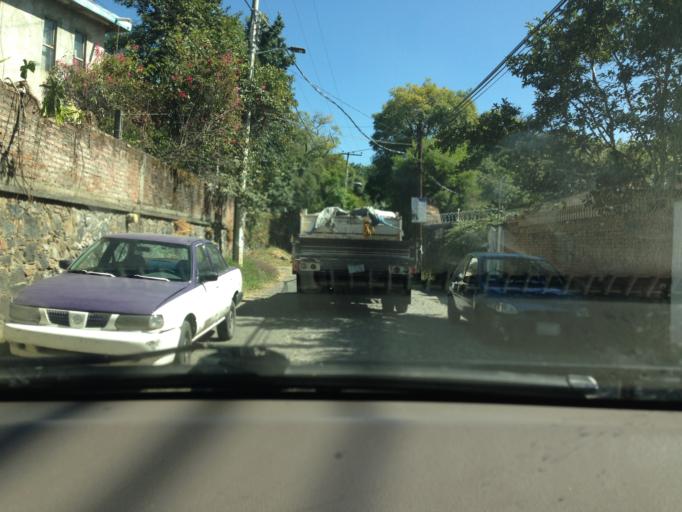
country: MX
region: Morelos
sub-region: Cuernavaca
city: Fraccionamiento Lomas de Ahuatlan
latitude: 18.9769
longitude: -99.2506
